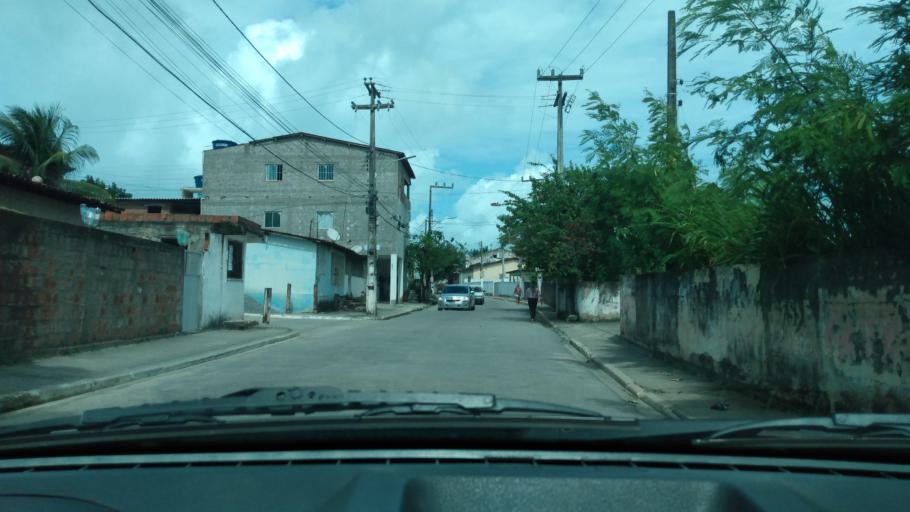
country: BR
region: Pernambuco
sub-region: Cabo De Santo Agostinho
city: Cabo
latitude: -8.3509
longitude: -34.9589
